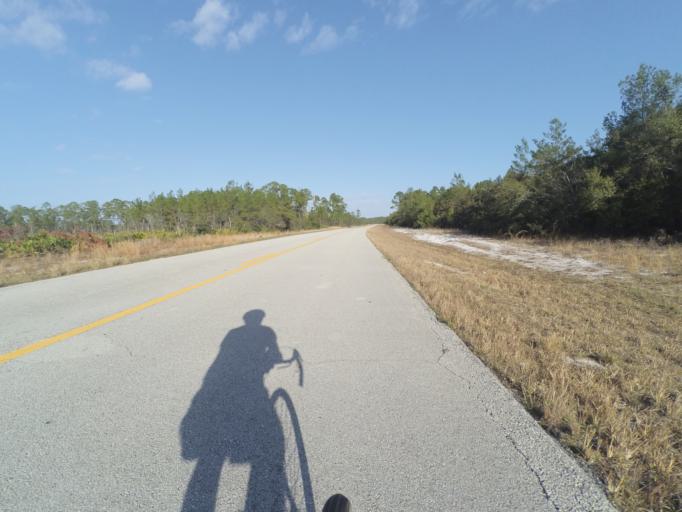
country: US
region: Florida
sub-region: Lake County
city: Astor
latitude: 29.1200
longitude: -81.5763
